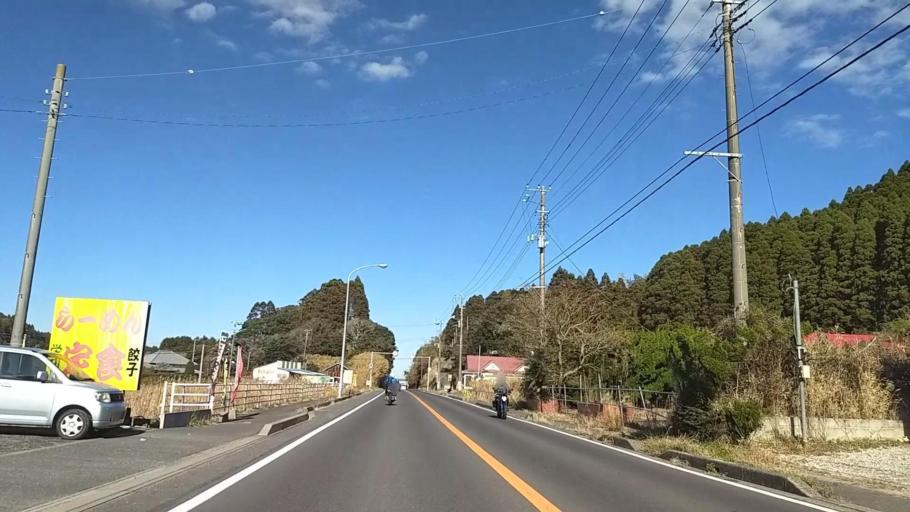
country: JP
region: Chiba
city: Ohara
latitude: 35.2140
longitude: 140.3767
